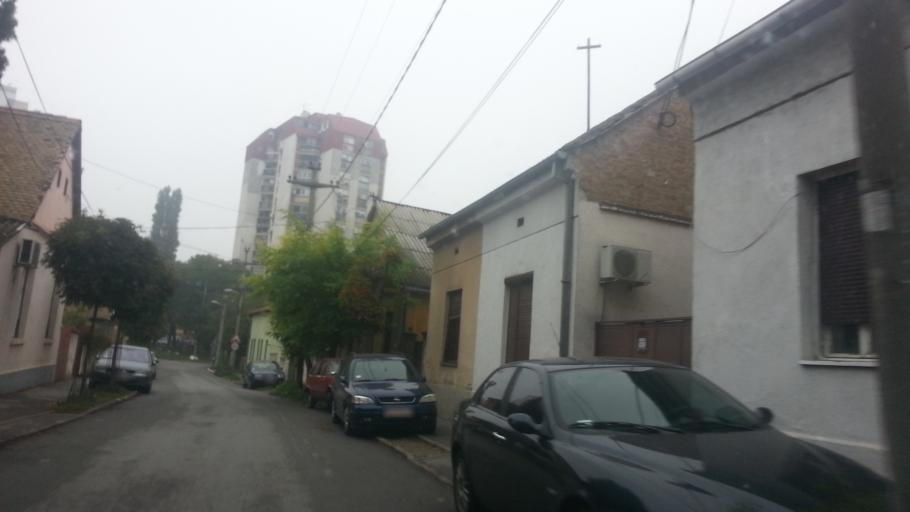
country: RS
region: Central Serbia
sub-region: Belgrade
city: Zemun
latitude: 44.8401
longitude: 20.3884
